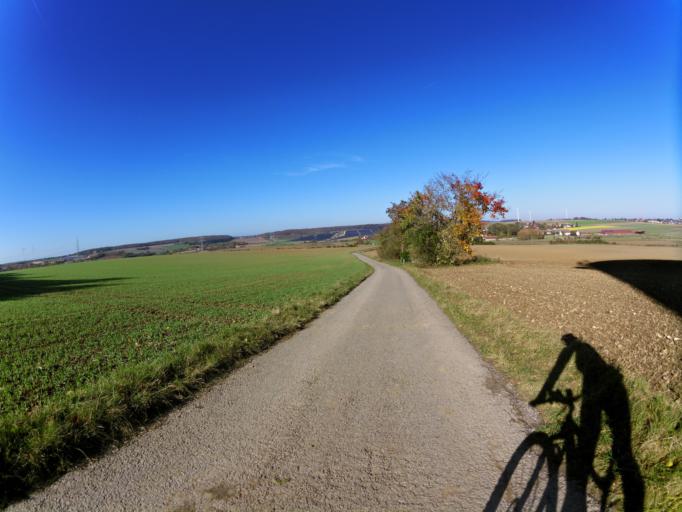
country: DE
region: Bavaria
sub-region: Regierungsbezirk Unterfranken
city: Kirchheim
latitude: 49.6670
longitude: 9.8807
